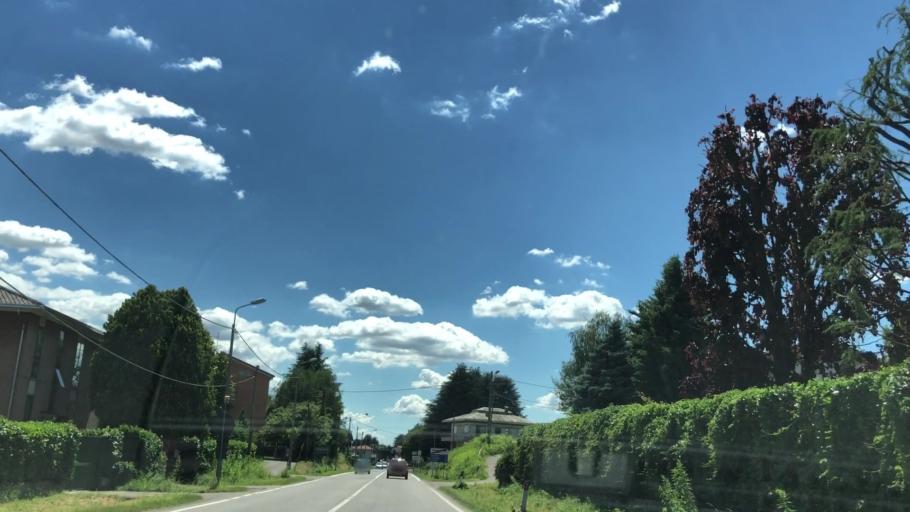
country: IT
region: Lombardy
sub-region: Provincia di Como
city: Lomazzo
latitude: 45.7077
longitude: 9.0372
